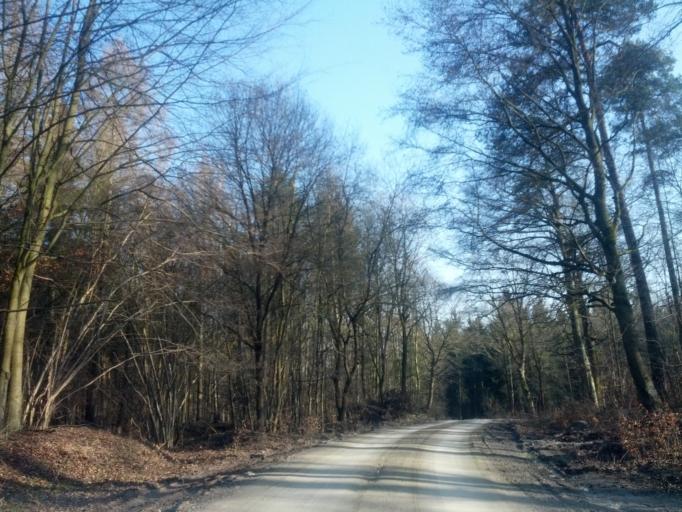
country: DE
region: Thuringia
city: Ebenshausen
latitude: 51.0814
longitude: 10.3069
